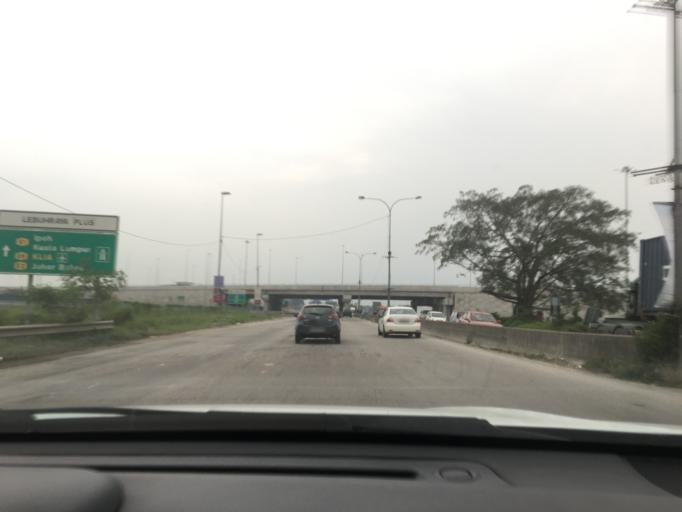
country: MY
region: Selangor
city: Klang
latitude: 3.0929
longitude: 101.4438
